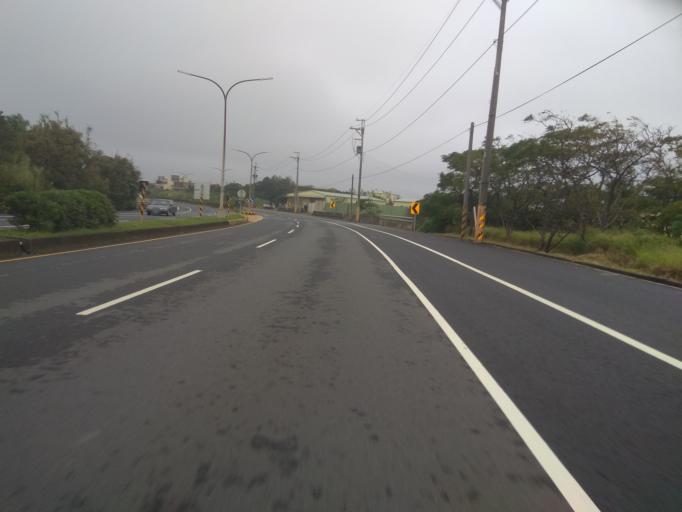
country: TW
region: Taiwan
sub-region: Hsinchu
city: Zhubei
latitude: 25.0324
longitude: 121.0738
